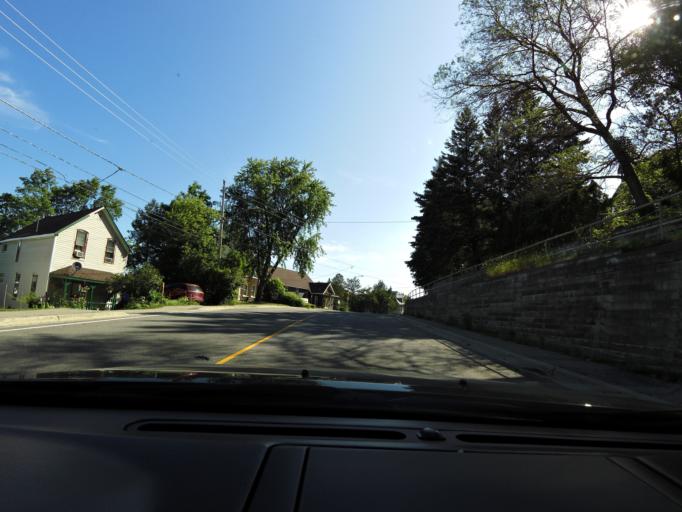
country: CA
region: Ontario
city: Huntsville
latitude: 45.3255
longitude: -79.2232
